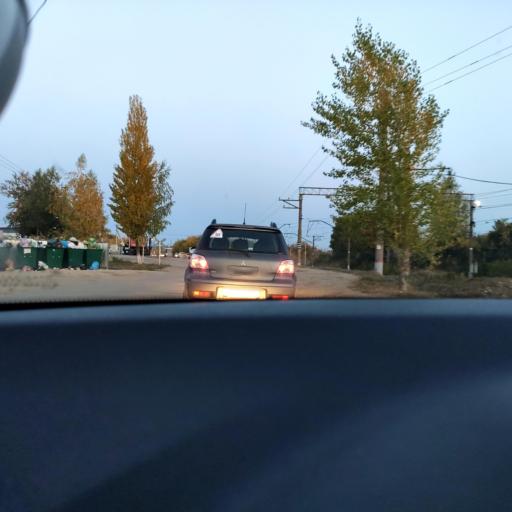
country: RU
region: Samara
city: Novosemeykino
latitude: 53.3693
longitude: 50.3548
